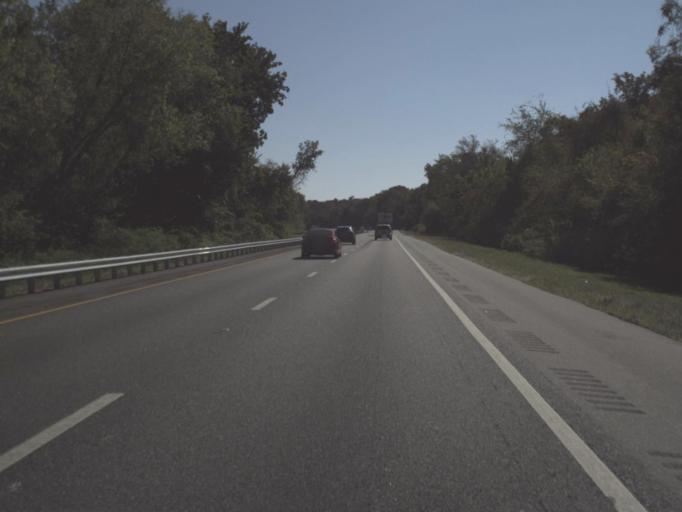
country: US
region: Florida
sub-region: Sumter County
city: Wildwood
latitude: 28.8538
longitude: -82.0874
